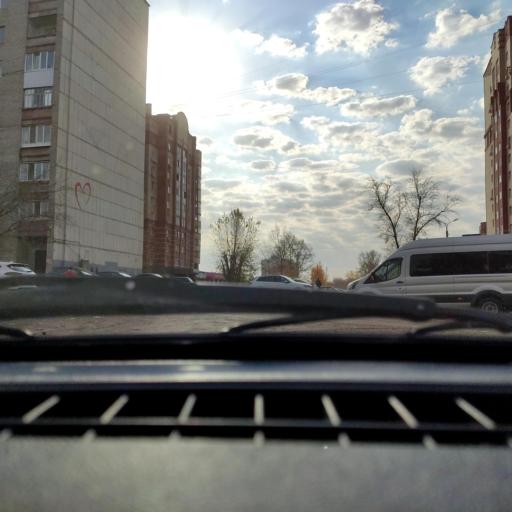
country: RU
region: Bashkortostan
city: Ufa
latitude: 54.7817
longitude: 56.1214
